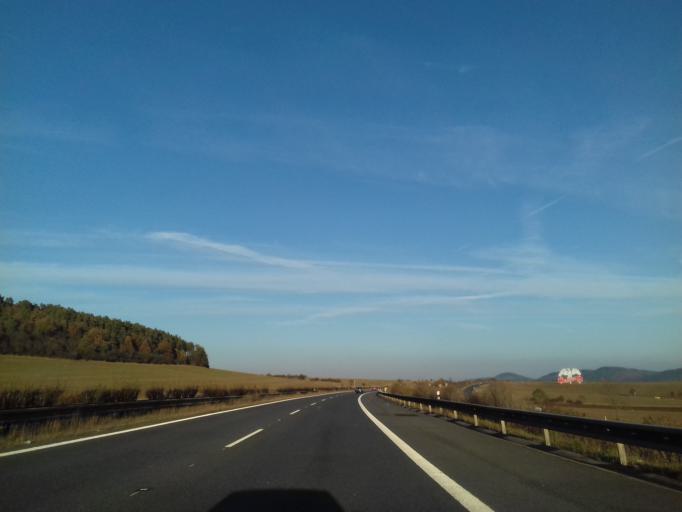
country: CZ
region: Central Bohemia
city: Zebrak
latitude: 49.8861
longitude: 13.9194
